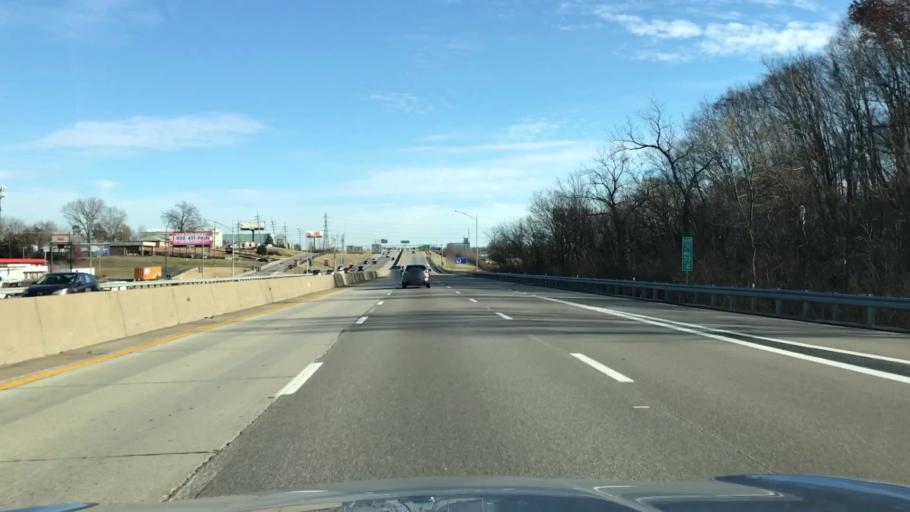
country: US
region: Missouri
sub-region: Saint Louis County
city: Spanish Lake
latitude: 38.7693
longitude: -90.2179
